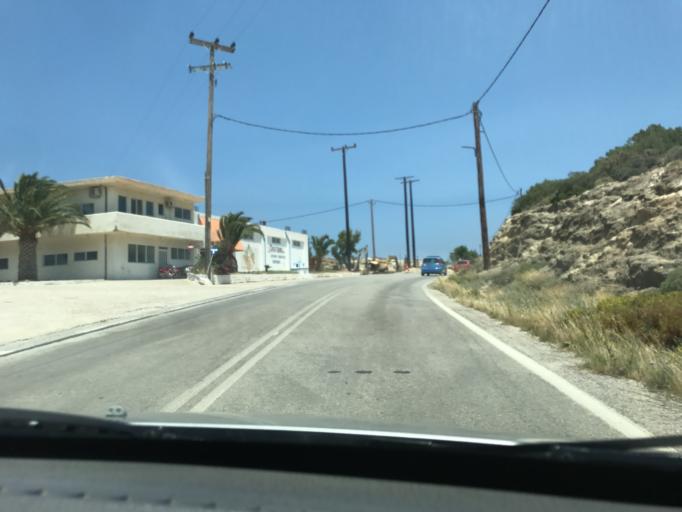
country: GR
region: South Aegean
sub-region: Nomos Dodekanisou
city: Karpathos
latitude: 35.4990
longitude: 27.2007
